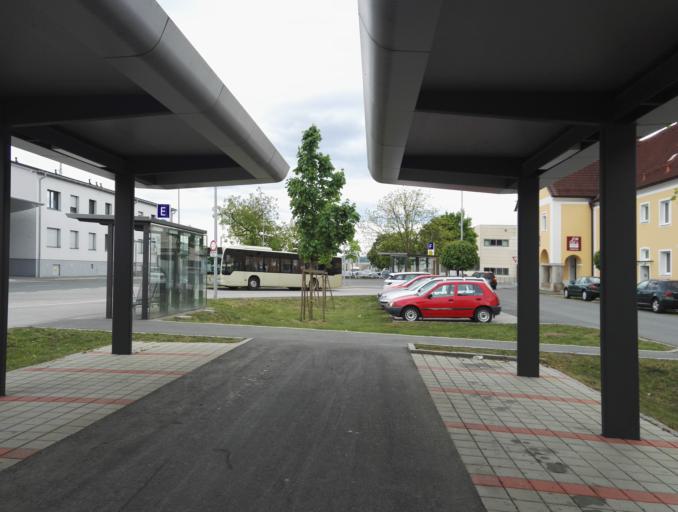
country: AT
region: Styria
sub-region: Politischer Bezirk Leibnitz
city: Leibnitz
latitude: 46.7802
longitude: 15.5464
